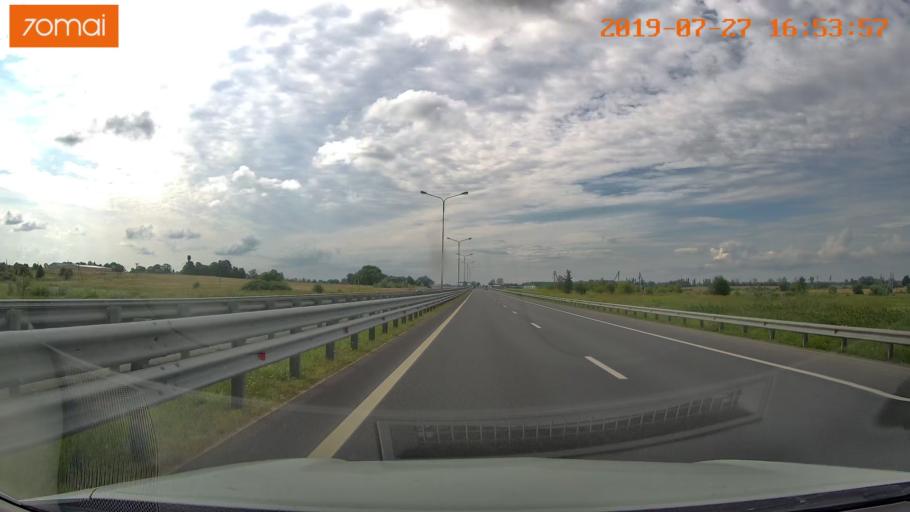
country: RU
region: Kaliningrad
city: Bol'shoe Isakovo
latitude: 54.6916
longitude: 20.8197
